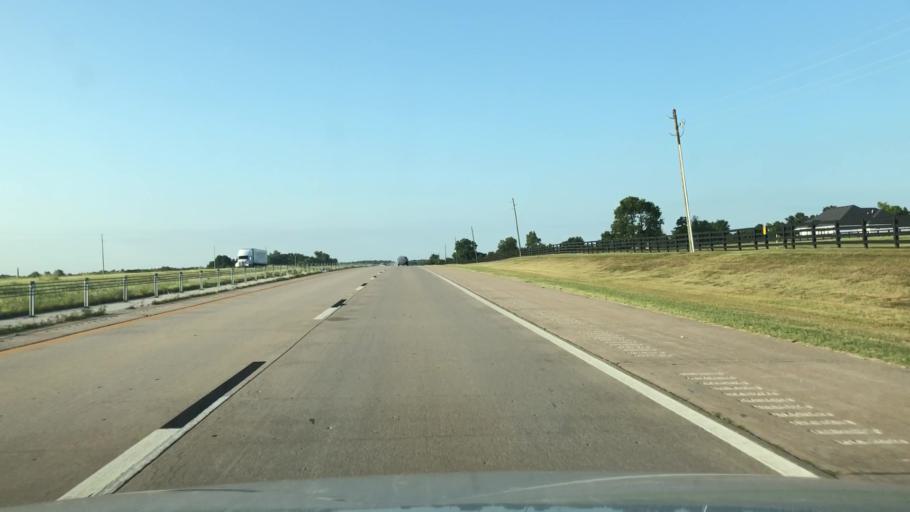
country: US
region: Oklahoma
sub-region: Osage County
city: Skiatook
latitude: 36.4657
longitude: -95.9207
